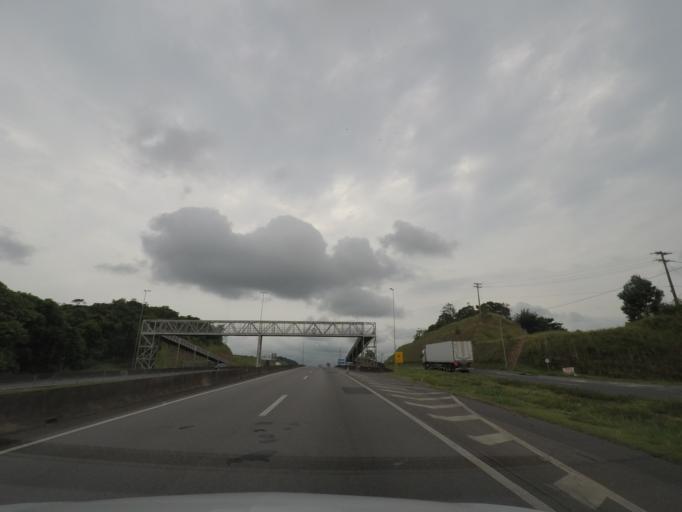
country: BR
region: Sao Paulo
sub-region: Juquia
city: Juquia
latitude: -24.3295
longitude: -47.6212
